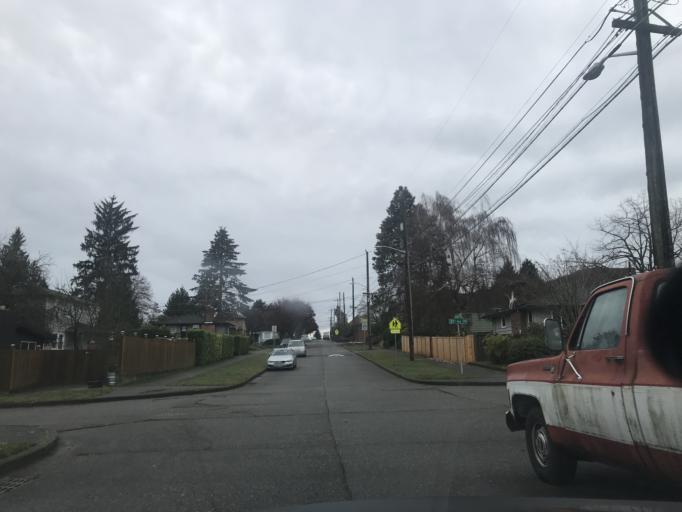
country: US
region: Washington
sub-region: King County
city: White Center
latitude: 47.5319
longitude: -122.3723
